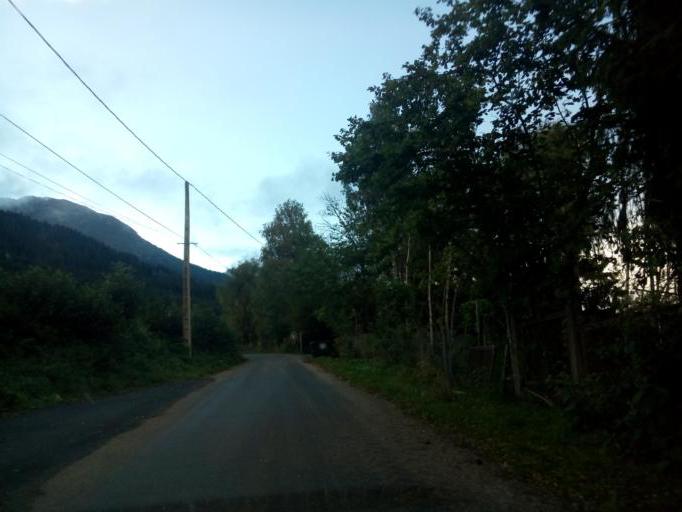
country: FR
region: Rhone-Alpes
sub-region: Departement de l'Isere
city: Le Champ-pres-Froges
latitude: 45.2486
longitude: 5.9747
